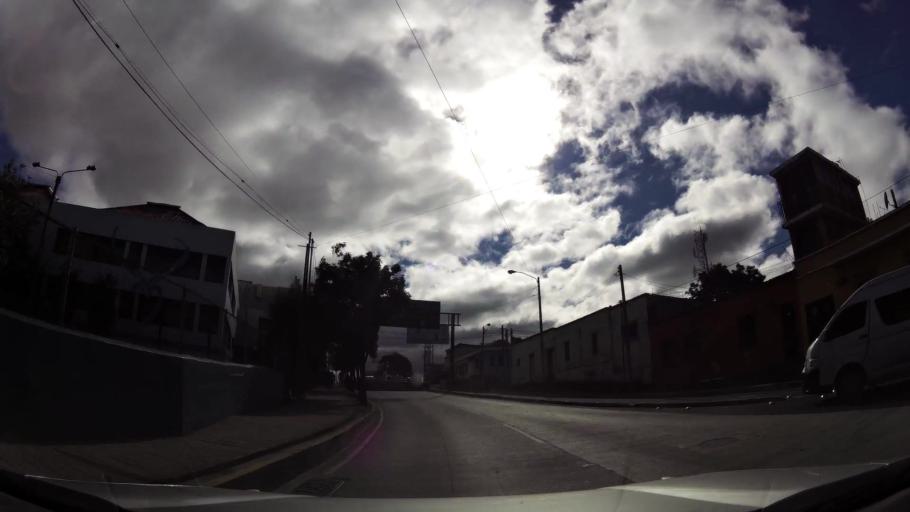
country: GT
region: Guatemala
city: Guatemala City
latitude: 14.6222
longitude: -90.5108
